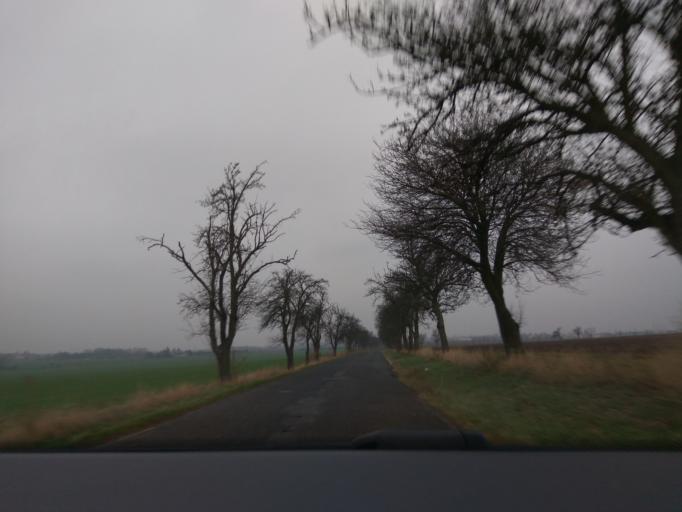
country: CZ
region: Praha
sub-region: Praha 19
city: Kbely
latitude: 50.1532
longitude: 14.5548
